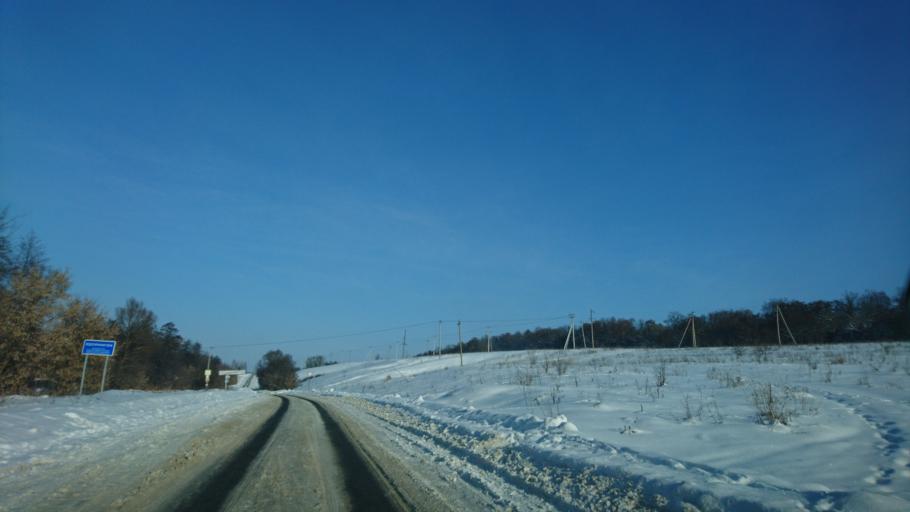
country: RU
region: Belgorod
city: Severnyy
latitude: 50.7260
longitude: 36.6118
